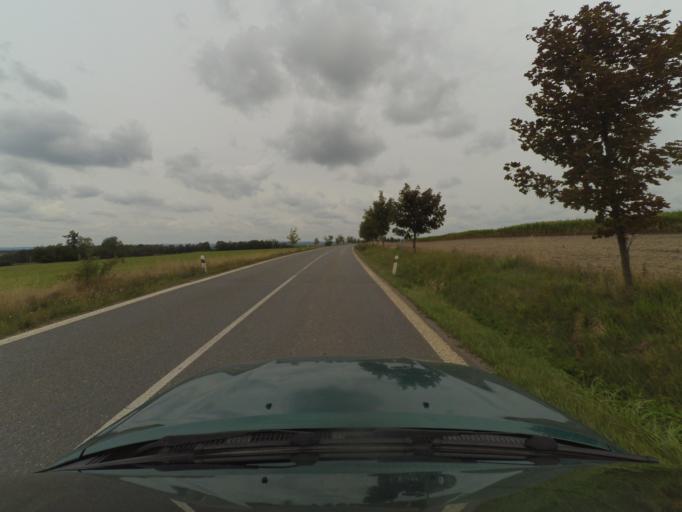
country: CZ
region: Central Bohemia
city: Pavlikov
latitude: 50.0718
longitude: 13.6807
